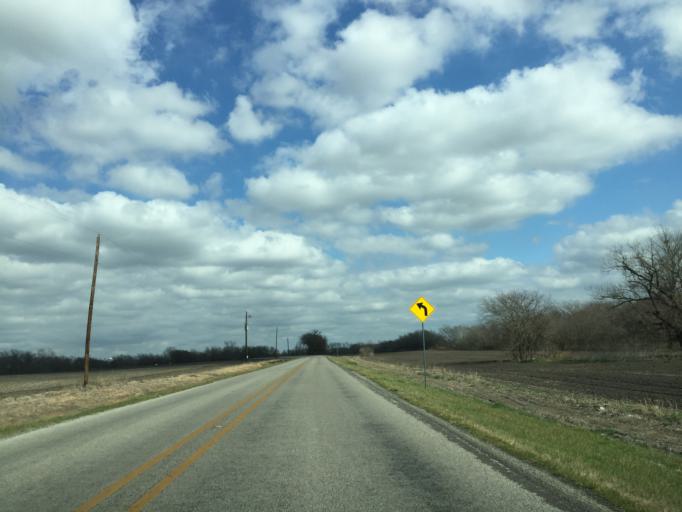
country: US
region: Texas
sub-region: Williamson County
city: Granger
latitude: 30.7080
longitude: -97.4642
